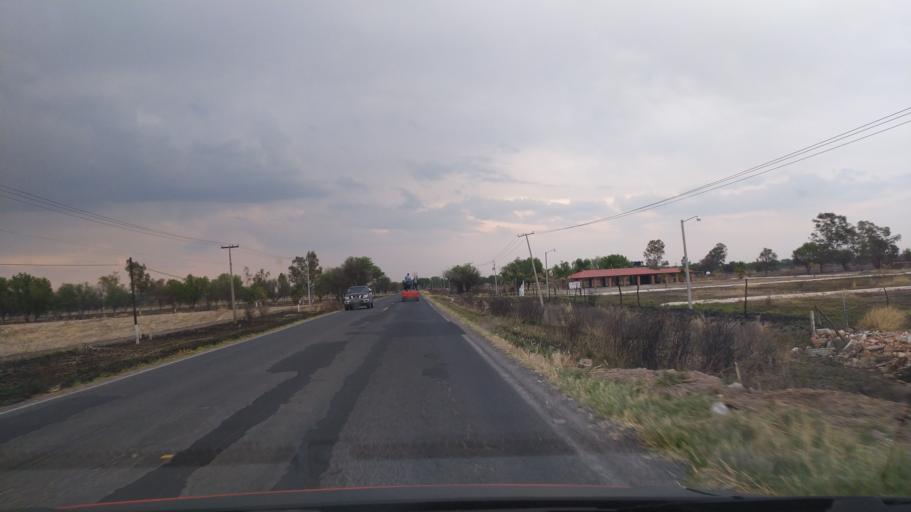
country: MX
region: Guanajuato
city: Ciudad Manuel Doblado
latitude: 20.7827
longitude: -101.9090
